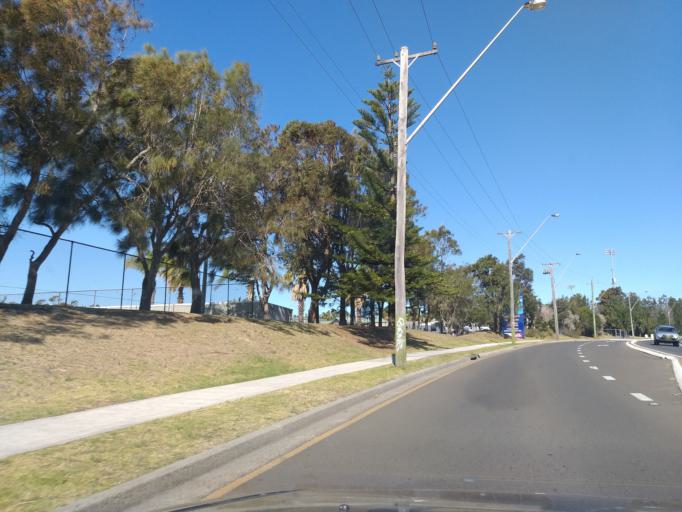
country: AU
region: New South Wales
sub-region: Wollongong
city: Corrimal
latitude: -34.3888
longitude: 150.9057
